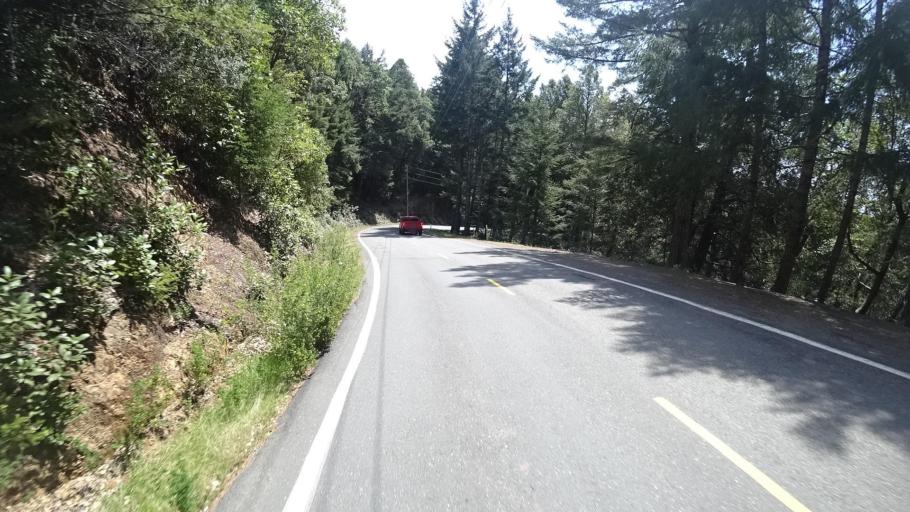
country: US
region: California
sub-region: Humboldt County
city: Redway
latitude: 40.0451
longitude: -124.0216
